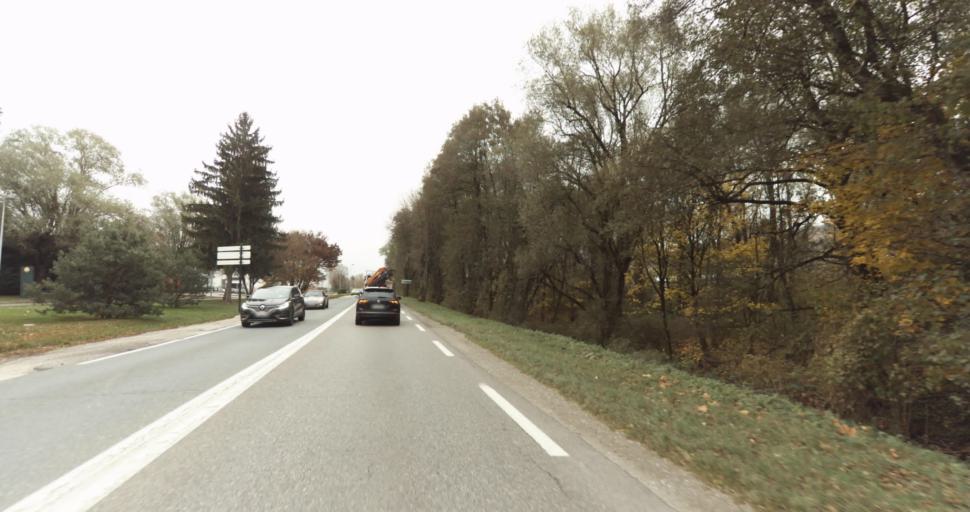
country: FR
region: Rhone-Alpes
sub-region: Departement de la Haute-Savoie
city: Poisy
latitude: 45.9363
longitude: 6.0742
